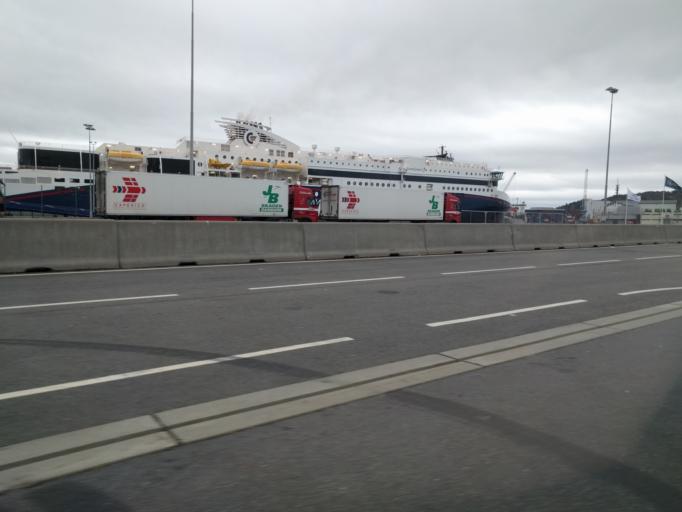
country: NO
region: Vest-Agder
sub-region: Kristiansand
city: Kristiansand
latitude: 58.1434
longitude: 7.9829
